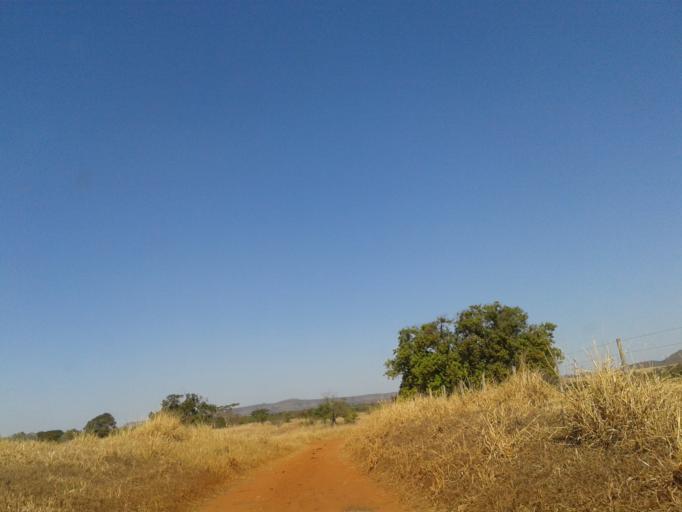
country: BR
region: Minas Gerais
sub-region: Santa Vitoria
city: Santa Vitoria
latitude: -19.1588
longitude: -50.0229
